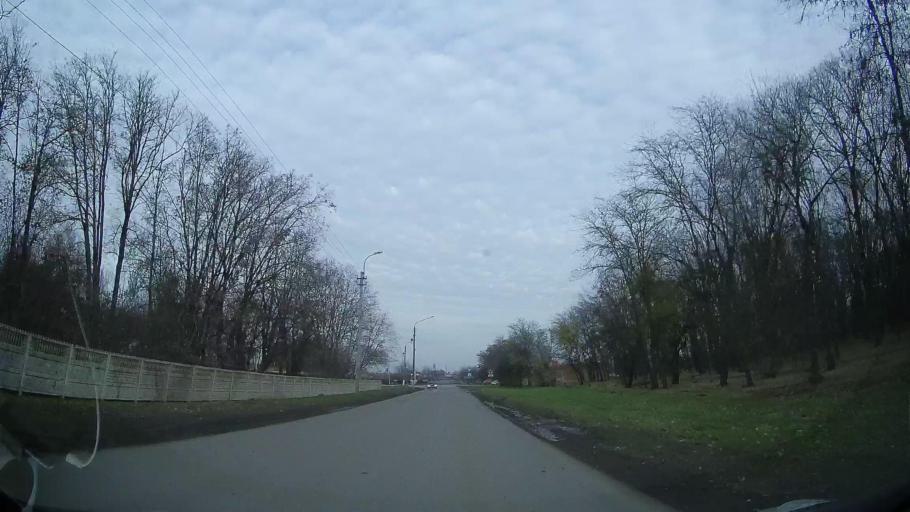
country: RU
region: Rostov
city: Zernograd
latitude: 46.8567
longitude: 40.3184
